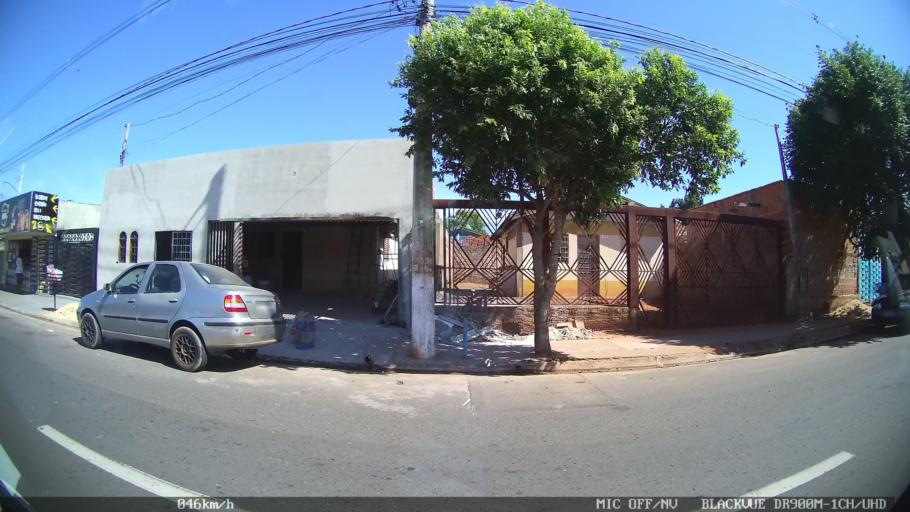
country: BR
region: Sao Paulo
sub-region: Sao Jose Do Rio Preto
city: Sao Jose do Rio Preto
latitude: -20.7430
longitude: -49.4089
